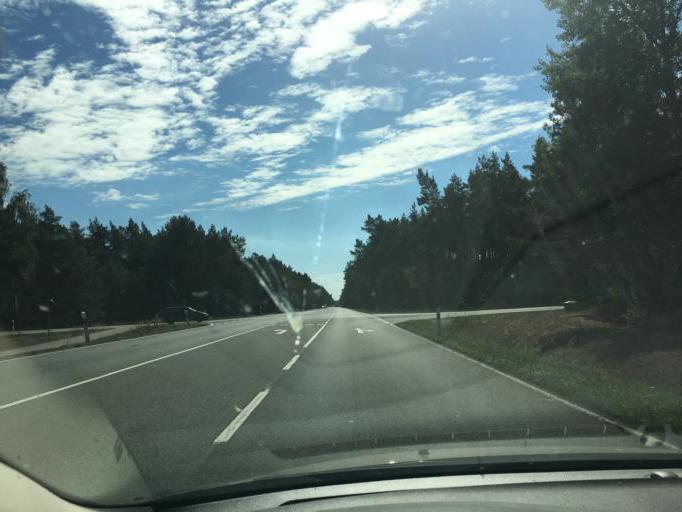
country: DE
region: Saxony-Anhalt
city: Seehausen
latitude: 52.8613
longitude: 11.7316
